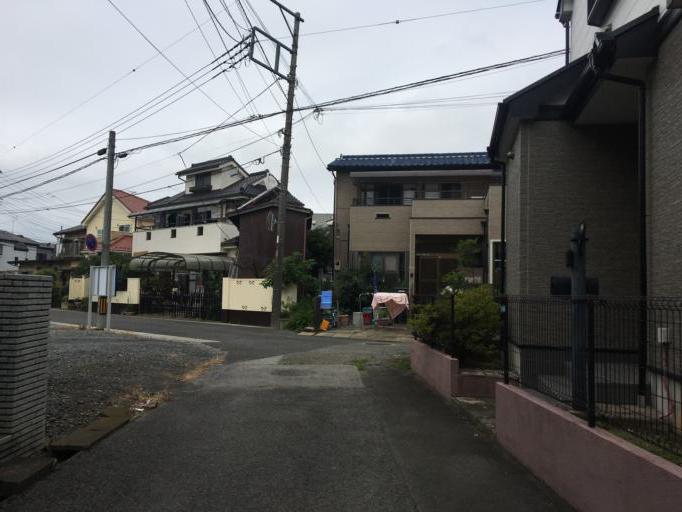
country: JP
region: Saitama
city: Ageoshimo
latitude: 35.9606
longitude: 139.5994
